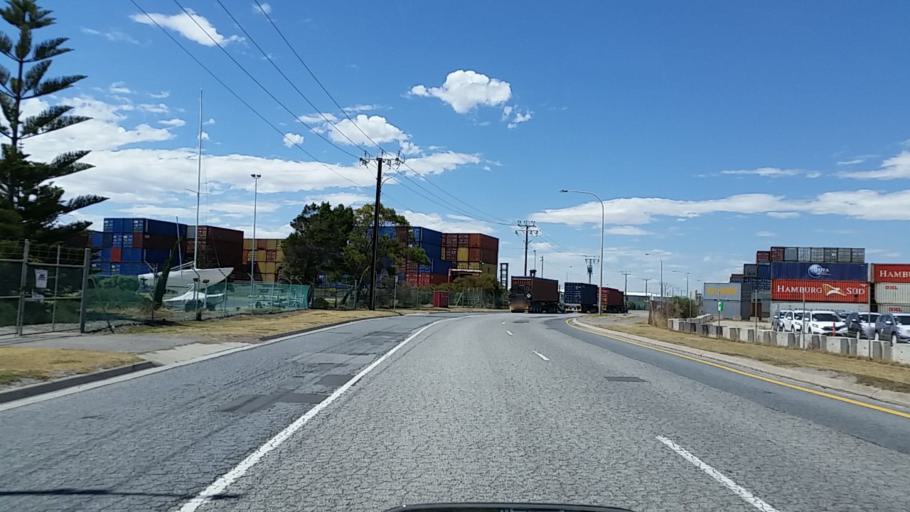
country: AU
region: South Australia
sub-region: Port Adelaide Enfield
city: Birkenhead
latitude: -34.7752
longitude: 138.4914
